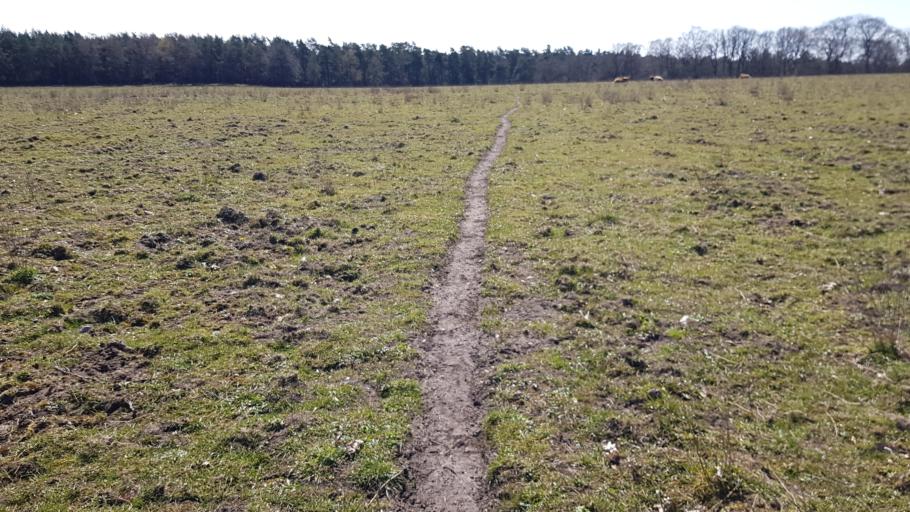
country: NL
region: Gelderland
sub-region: Gemeente Rozendaal
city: Rozendaal
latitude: 52.0762
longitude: 5.9558
